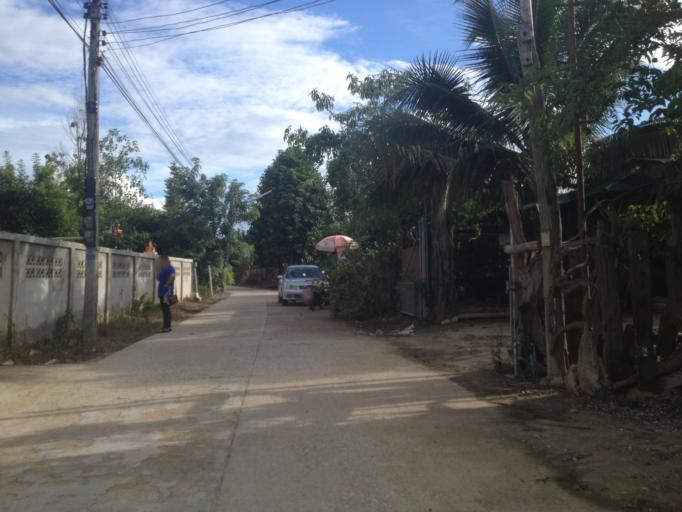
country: TH
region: Chiang Mai
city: Hang Dong
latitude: 18.6836
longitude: 98.8944
